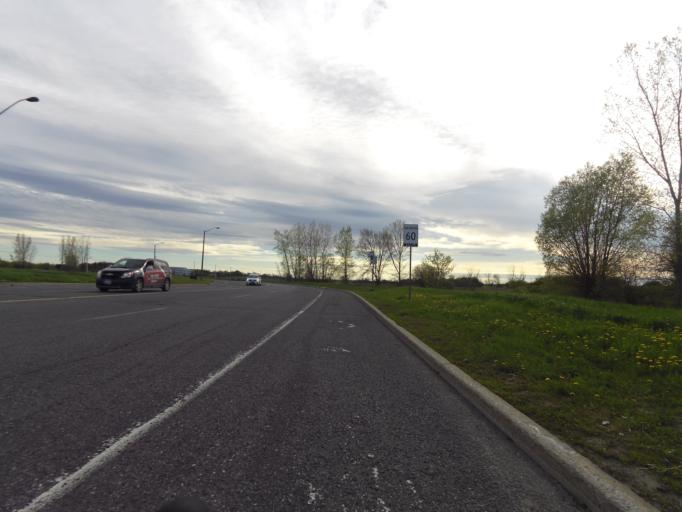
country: CA
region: Ontario
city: Ottawa
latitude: 45.3015
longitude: -75.7057
